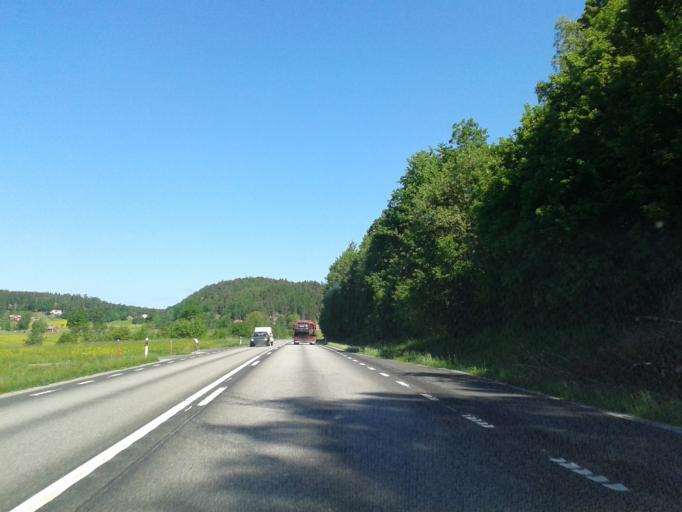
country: SE
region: Vaestra Goetaland
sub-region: Orust
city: Henan
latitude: 58.1983
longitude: 11.6898
